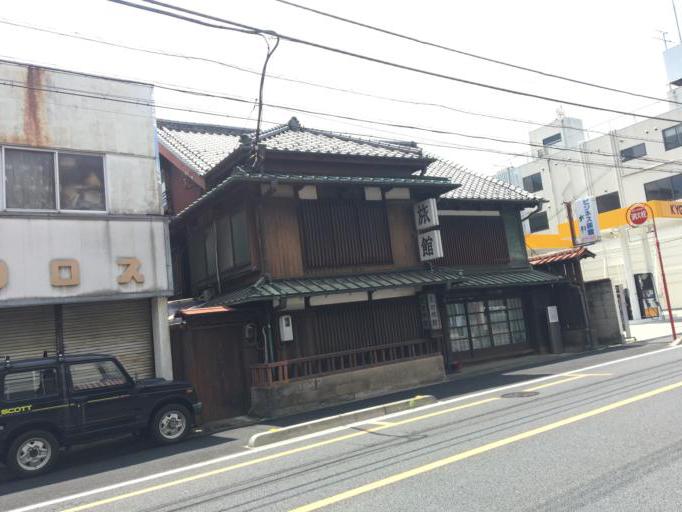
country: JP
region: Saitama
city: Okegawa
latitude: 35.9991
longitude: 139.5672
